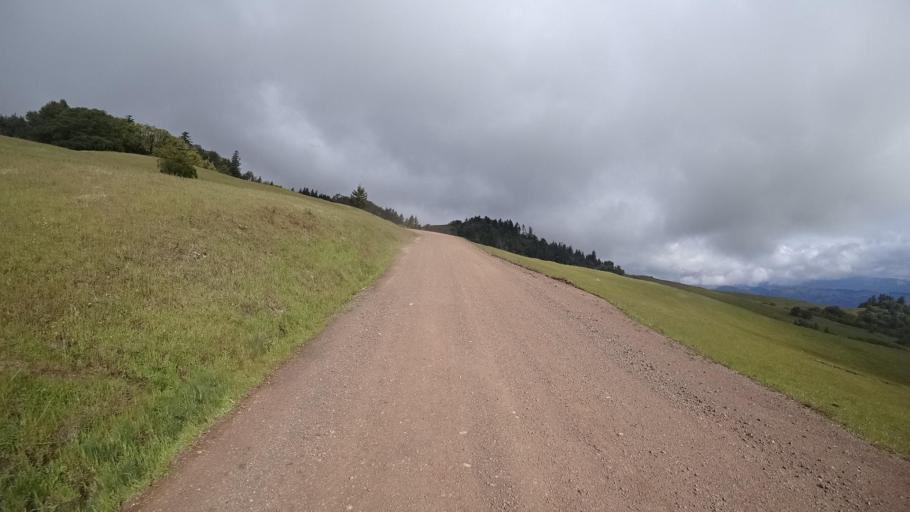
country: US
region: California
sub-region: Humboldt County
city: Redway
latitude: 40.2006
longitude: -123.6958
